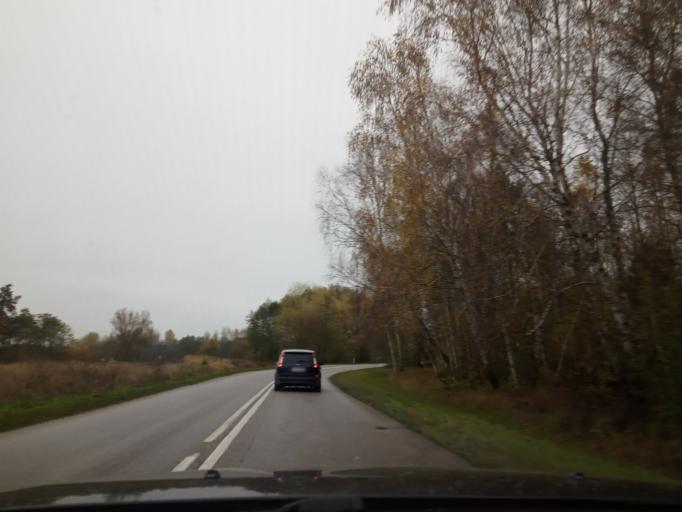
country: PL
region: Swietokrzyskie
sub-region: Powiat jedrzejowski
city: Jedrzejow
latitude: 50.5141
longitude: 20.3213
